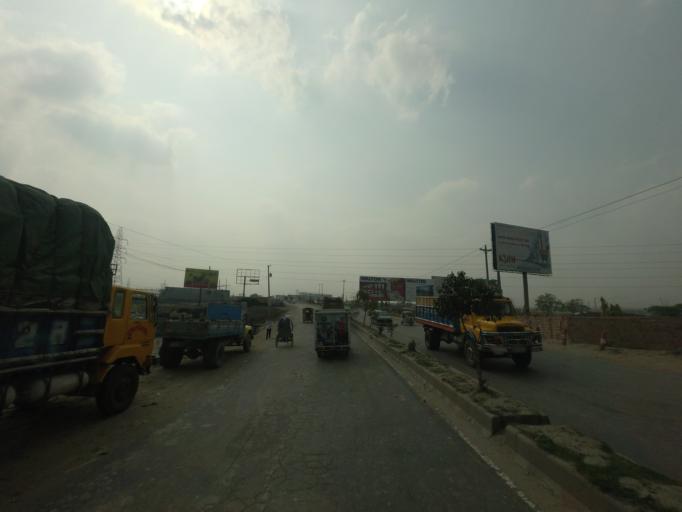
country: BD
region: Dhaka
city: Azimpur
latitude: 23.7900
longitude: 90.3235
